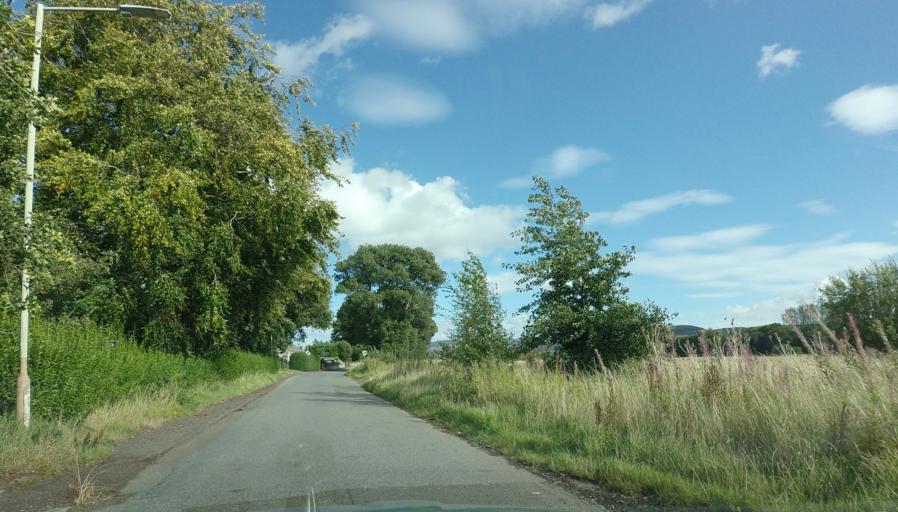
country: GB
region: Scotland
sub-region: Perth and Kinross
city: Bridge of Earn
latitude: 56.3459
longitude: -3.3916
